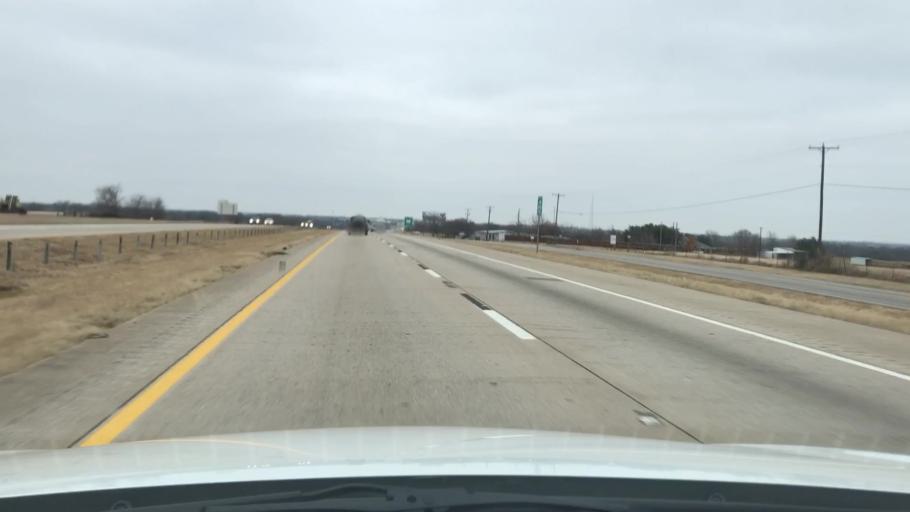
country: US
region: Texas
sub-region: Denton County
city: Sanger
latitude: 33.4547
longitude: -97.1642
